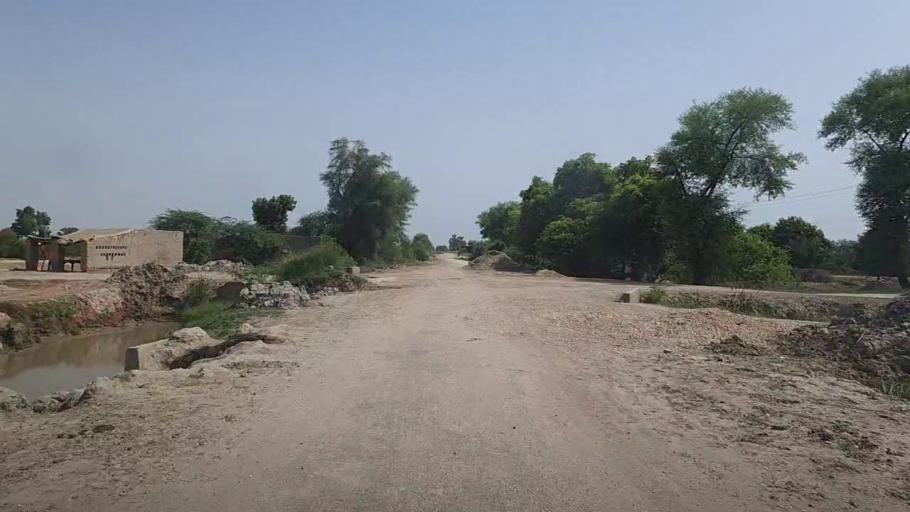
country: PK
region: Sindh
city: Pad Idan
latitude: 26.8192
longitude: 68.3278
